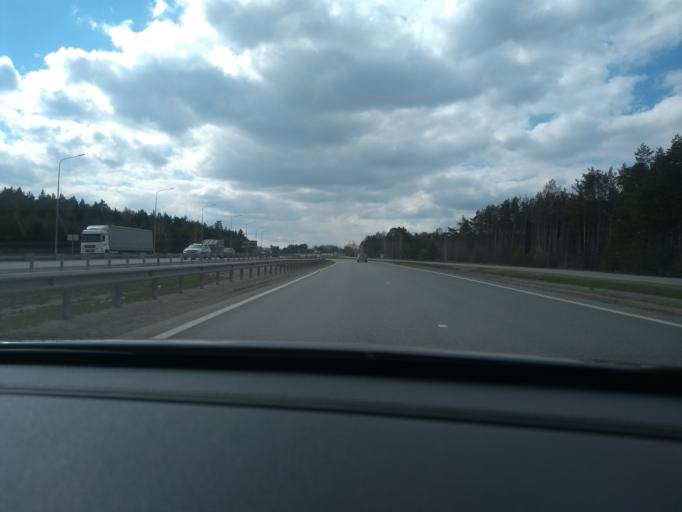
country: RU
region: Tatarstan
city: Yelabuga
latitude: 55.7815
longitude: 52.1900
